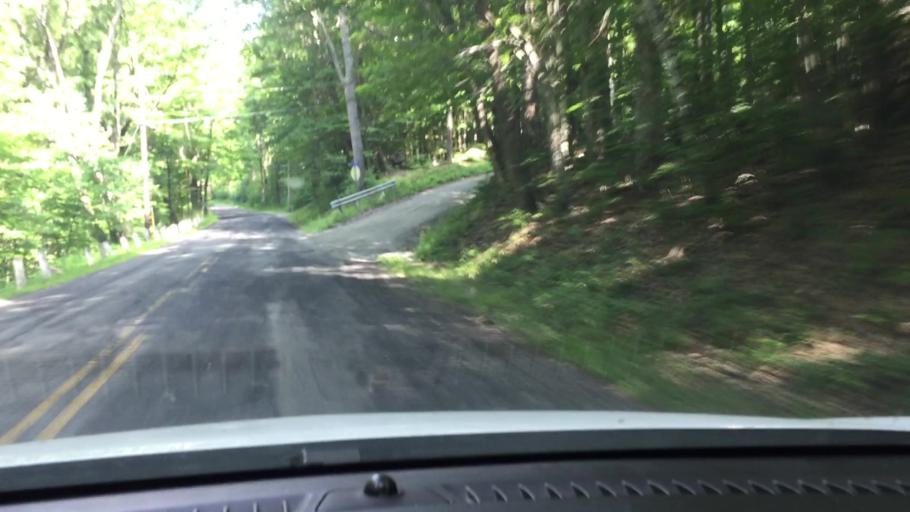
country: US
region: Massachusetts
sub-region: Berkshire County
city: Otis
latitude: 42.1901
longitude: -73.1541
